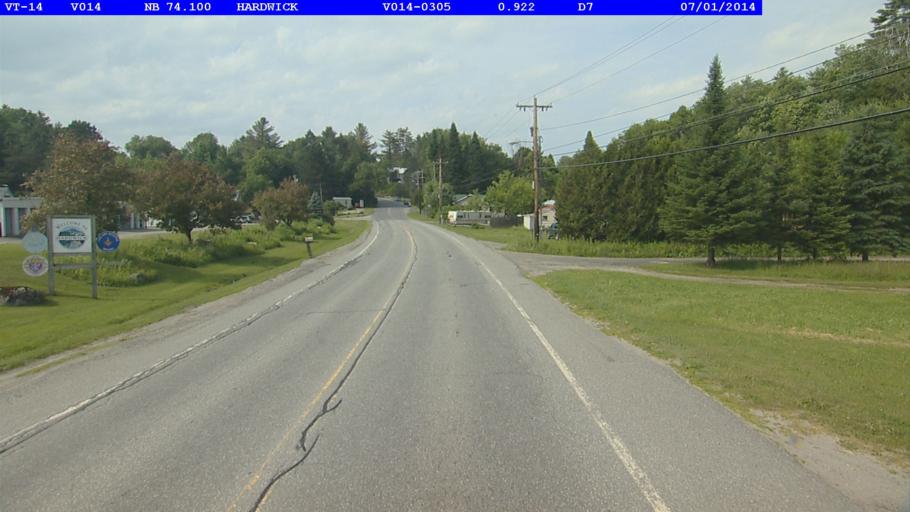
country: US
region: Vermont
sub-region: Caledonia County
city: Hardwick
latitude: 44.4969
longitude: -72.3719
